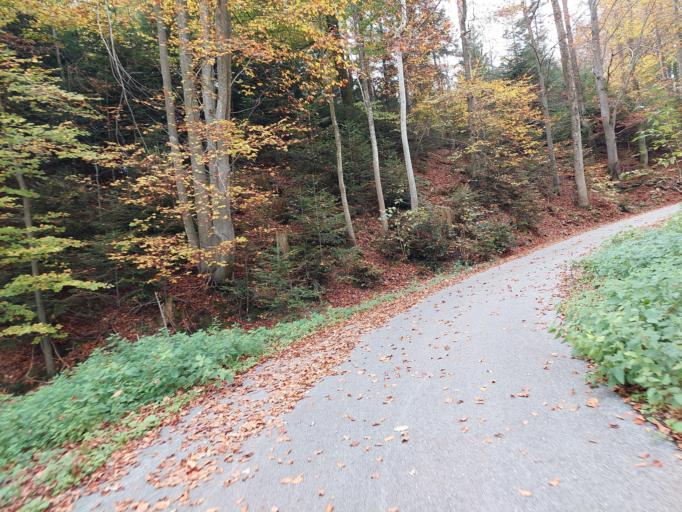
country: AT
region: Tyrol
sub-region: Politischer Bezirk Kufstein
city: Angath
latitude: 47.4931
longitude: 12.0531
